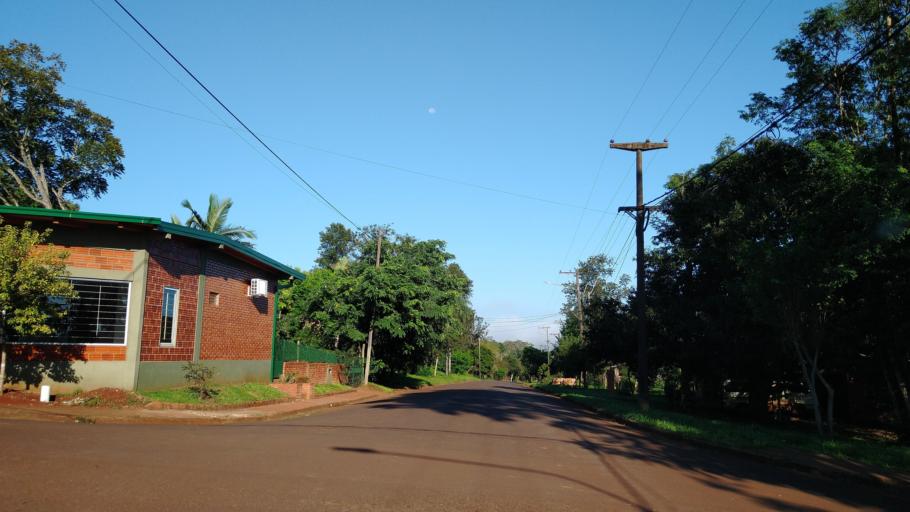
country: AR
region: Misiones
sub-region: Departamento de Montecarlo
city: Montecarlo
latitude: -26.5650
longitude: -54.7656
